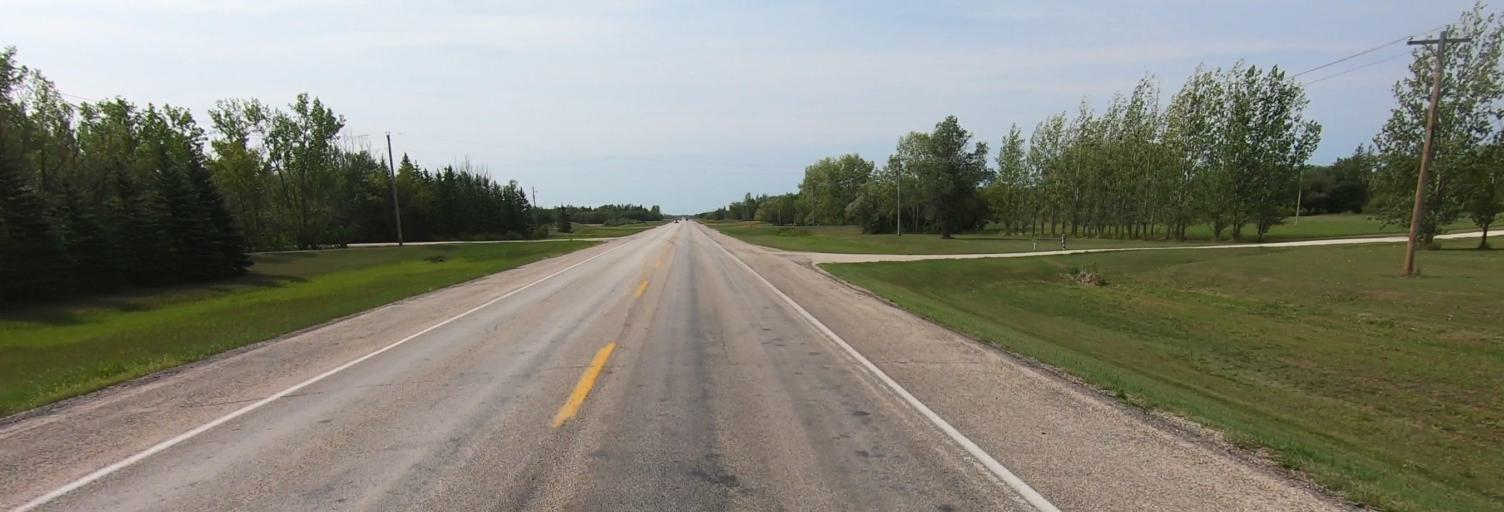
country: CA
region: Manitoba
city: Niverville
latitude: 49.6295
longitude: -97.1114
